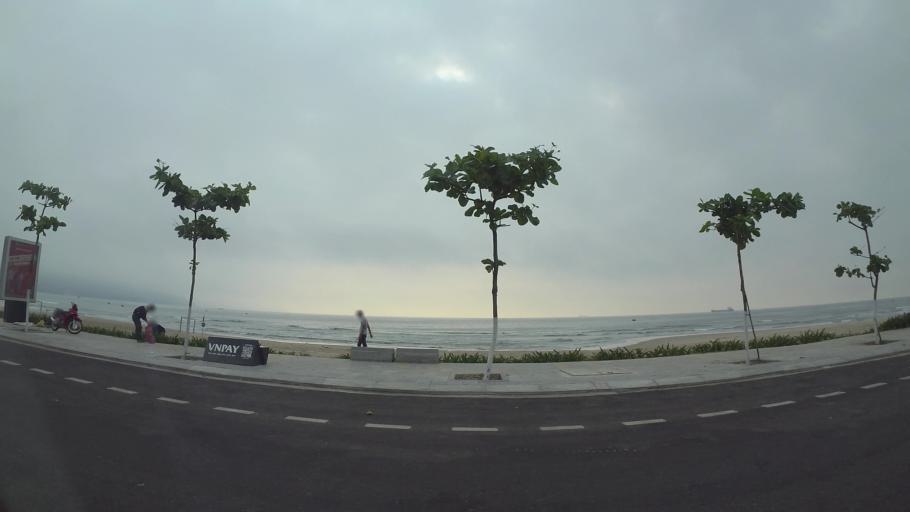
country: VN
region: Da Nang
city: Son Tra
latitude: 16.0830
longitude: 108.2478
